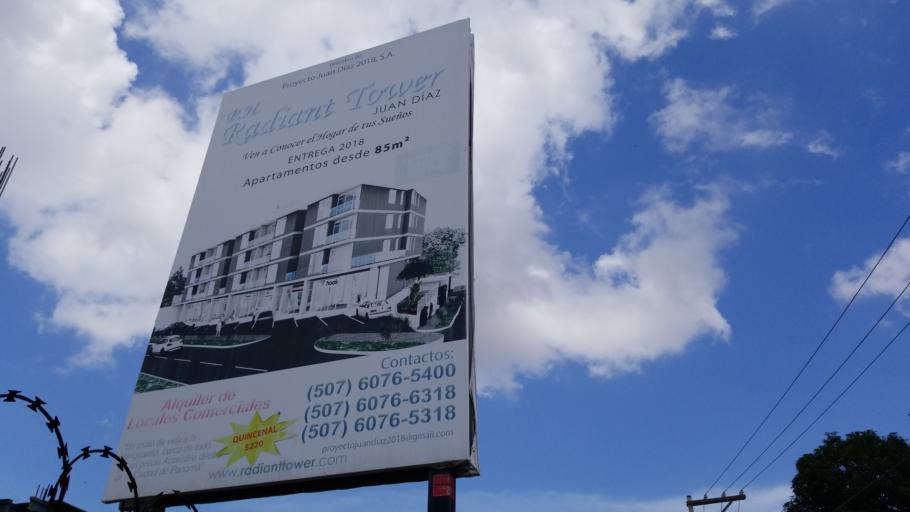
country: PA
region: Panama
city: San Miguelito
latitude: 9.0459
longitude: -79.4327
